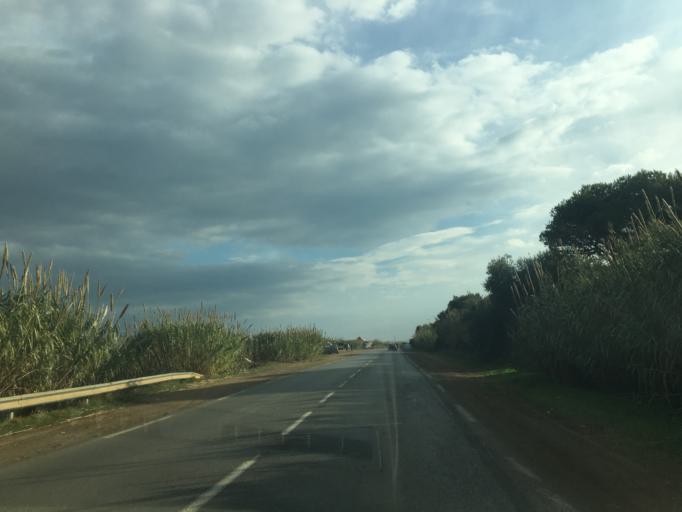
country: DZ
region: Tipaza
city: Tipasa
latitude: 36.5894
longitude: 2.4958
